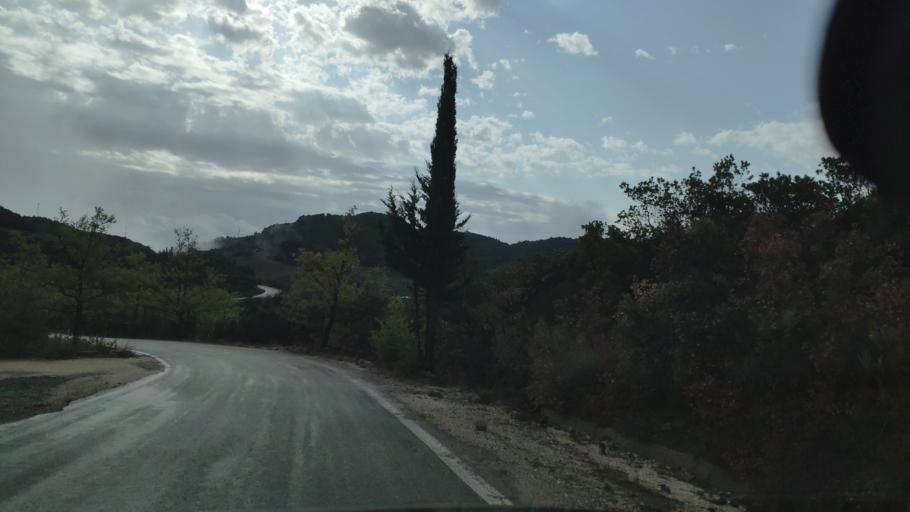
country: GR
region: West Greece
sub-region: Nomos Aitolias kai Akarnanias
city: Sardinia
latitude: 38.8733
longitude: 21.2754
